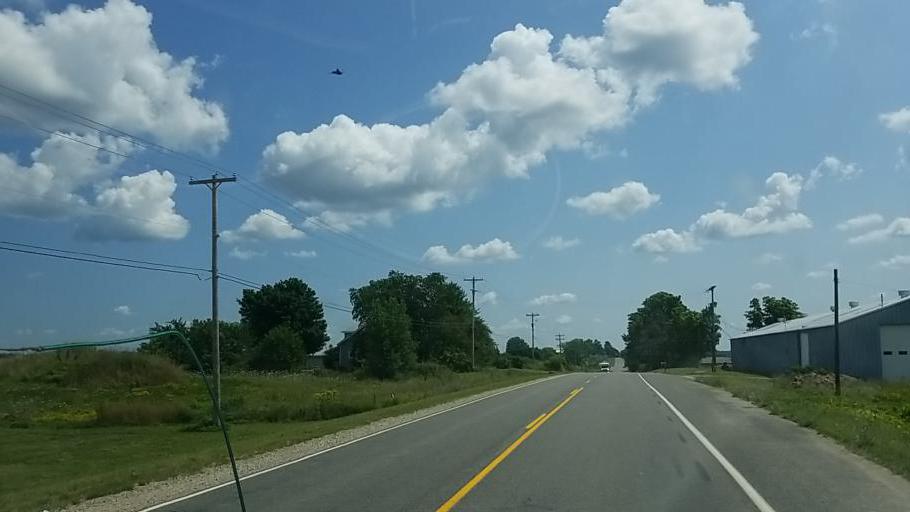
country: US
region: Michigan
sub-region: Kent County
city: Sparta
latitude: 43.1179
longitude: -85.7781
